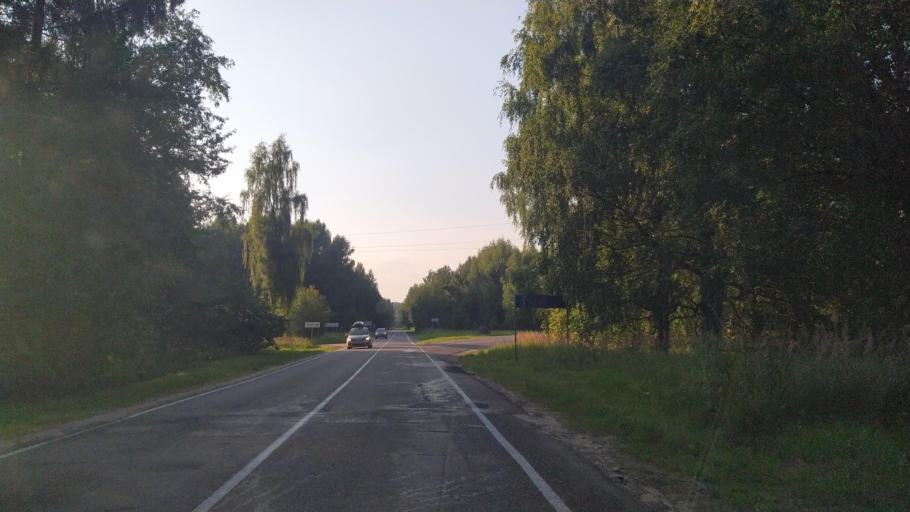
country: RU
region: Pskov
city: Pushkinskiye Gory
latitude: 57.0372
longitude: 28.9121
